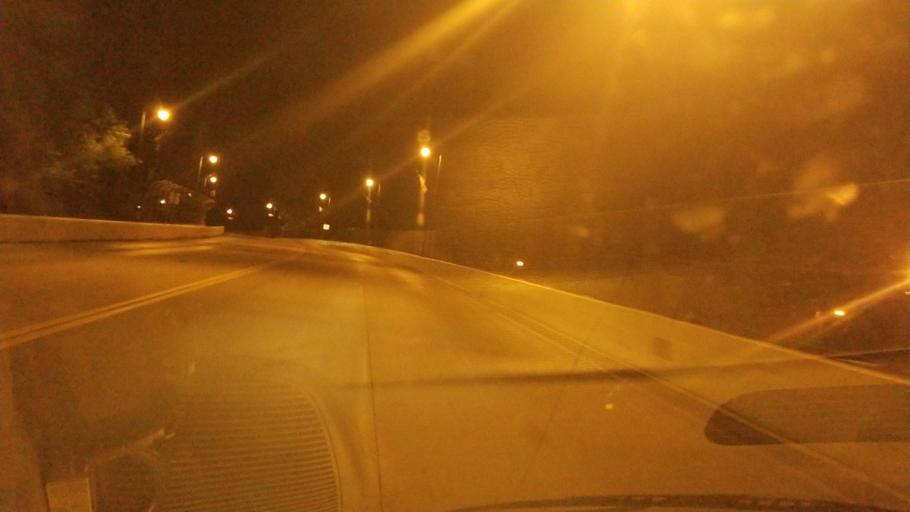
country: US
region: Ohio
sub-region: Trumbull County
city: Niles
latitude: 41.1761
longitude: -80.7658
